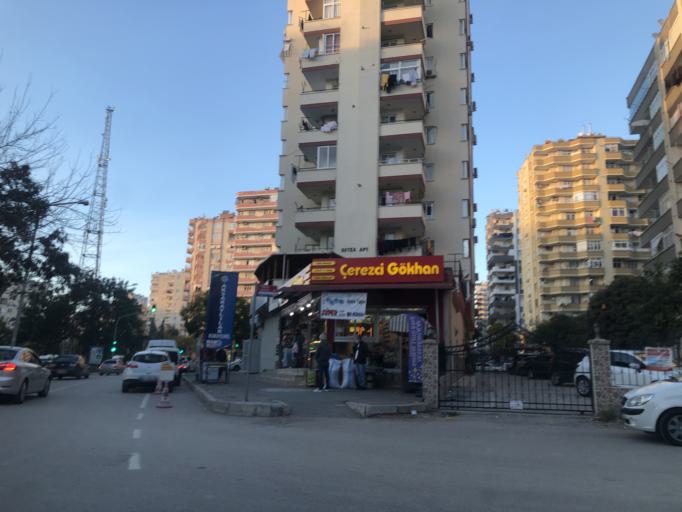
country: TR
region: Adana
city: Adana
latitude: 37.0455
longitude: 35.2966
